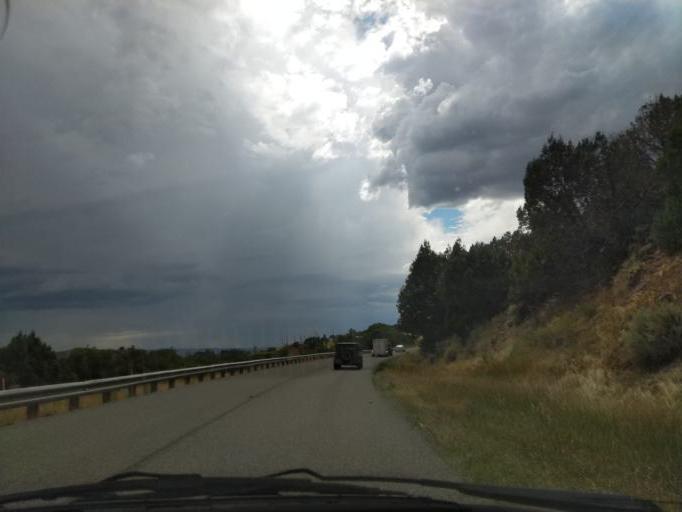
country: US
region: Colorado
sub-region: Delta County
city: Paonia
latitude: 38.8934
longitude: -107.5759
